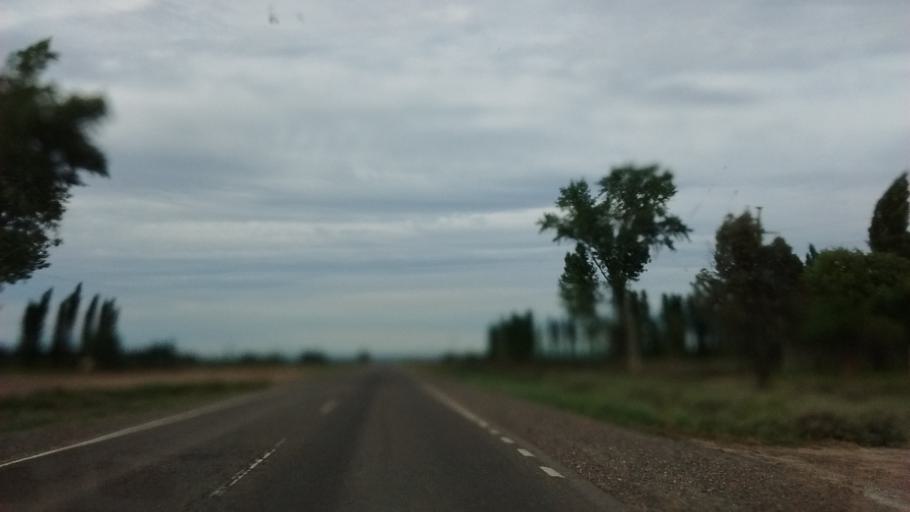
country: AR
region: Rio Negro
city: Catriel
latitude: -37.9219
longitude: -67.8741
